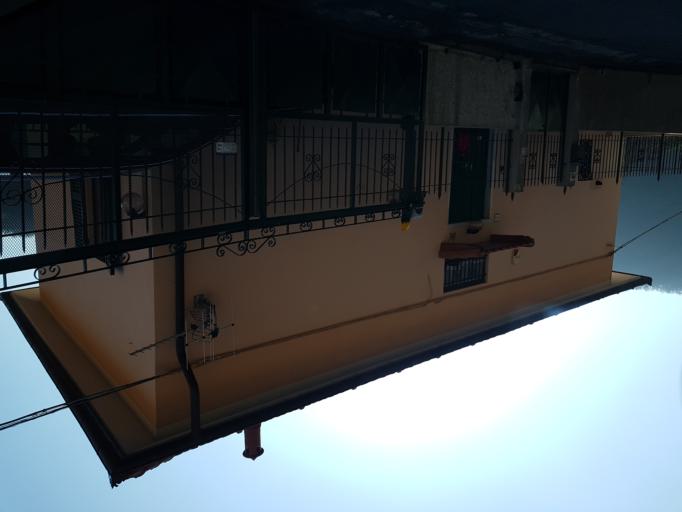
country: IT
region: Liguria
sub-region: Provincia di Genova
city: Manesseno
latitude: 44.4566
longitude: 8.9143
